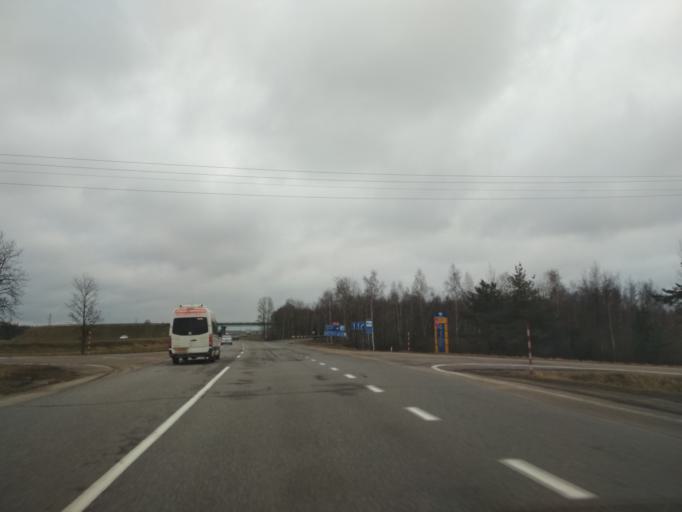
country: BY
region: Minsk
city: Dukora
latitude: 53.6616
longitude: 27.9427
